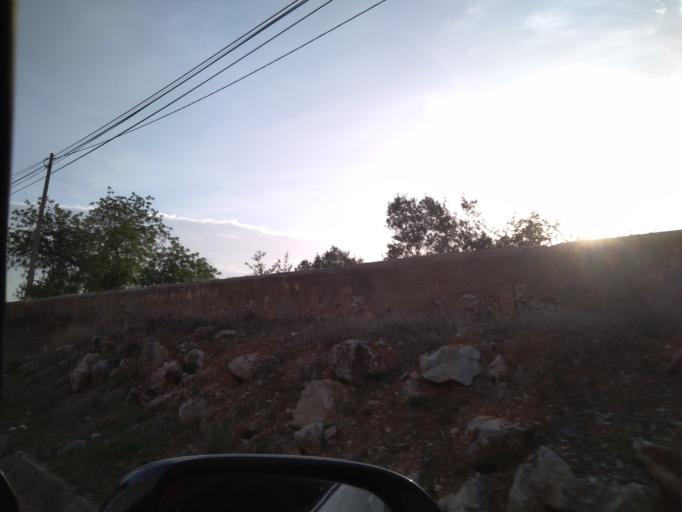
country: PT
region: Faro
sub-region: Faro
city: Santa Barbara de Nexe
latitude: 37.0934
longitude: -7.9626
